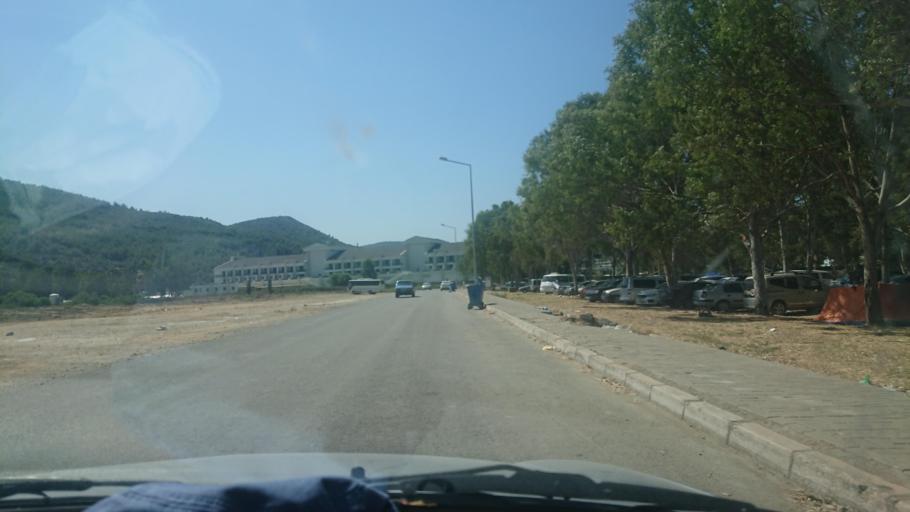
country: TR
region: Aydin
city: Kusadasi
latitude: 37.9383
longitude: 27.2780
